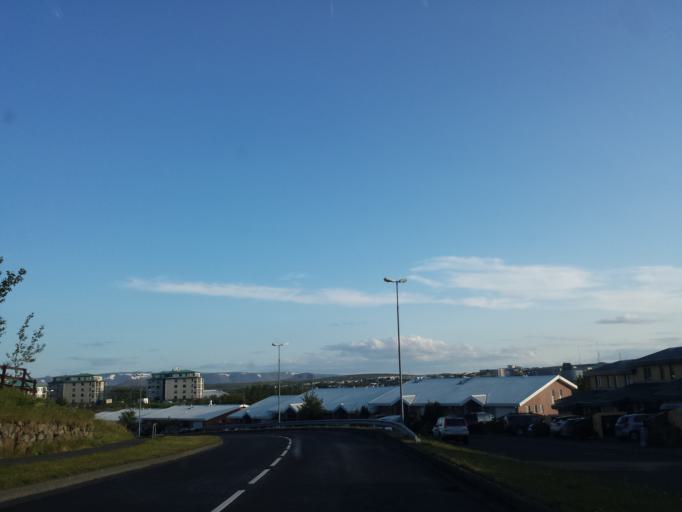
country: IS
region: Capital Region
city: Mosfellsbaer
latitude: 64.1076
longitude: -21.7887
